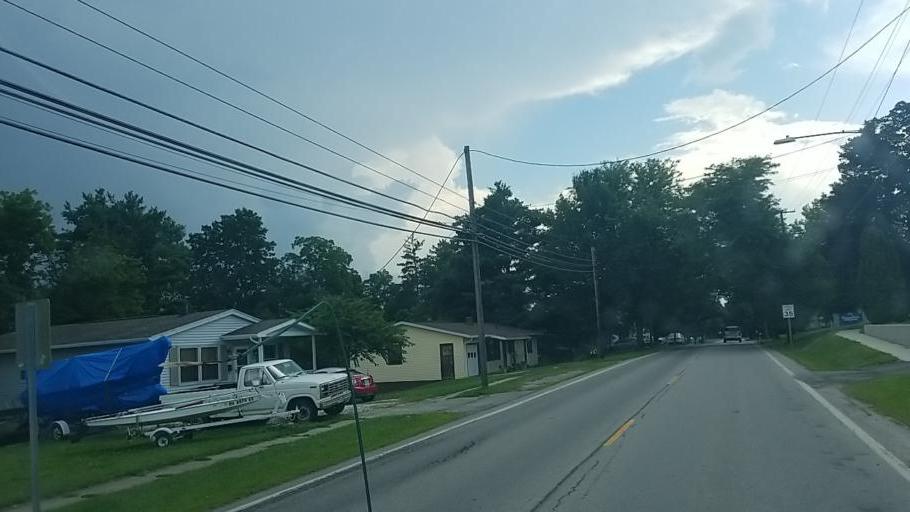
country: US
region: Ohio
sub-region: Medina County
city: Lodi
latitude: 41.0381
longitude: -82.0070
